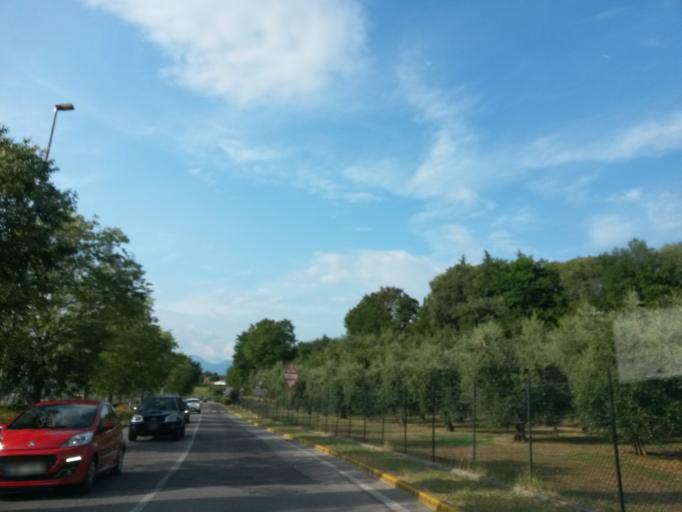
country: IT
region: Lombardy
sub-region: Provincia di Brescia
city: Padenghe sul Garda
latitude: 45.5090
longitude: 10.5107
